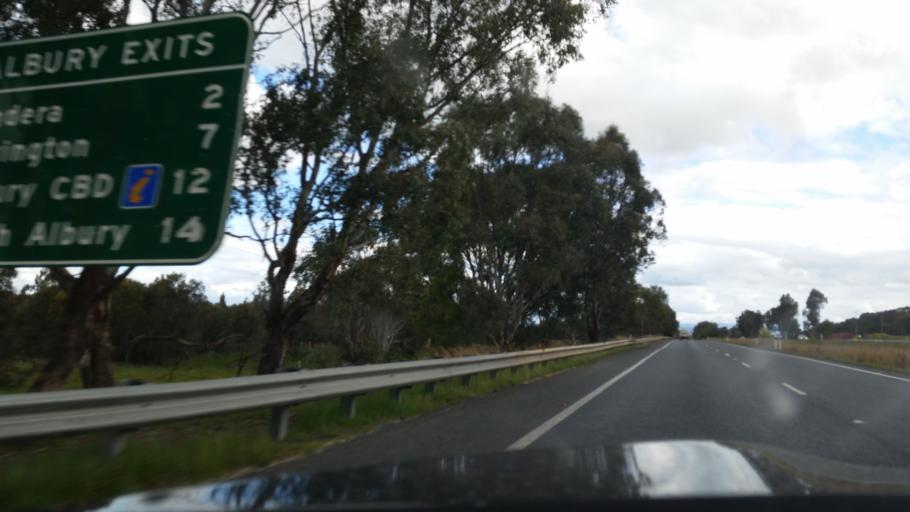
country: AU
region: New South Wales
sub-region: Albury Municipality
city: Lavington
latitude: -35.9815
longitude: 147.0000
